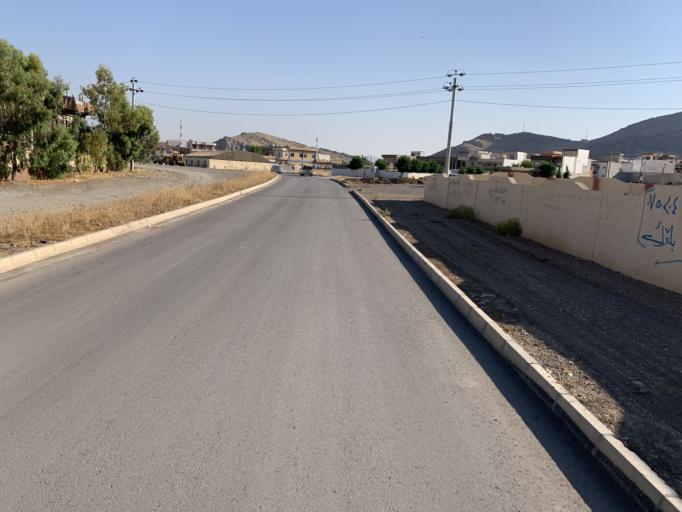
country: IQ
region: As Sulaymaniyah
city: Raniye
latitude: 36.2412
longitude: 44.8713
